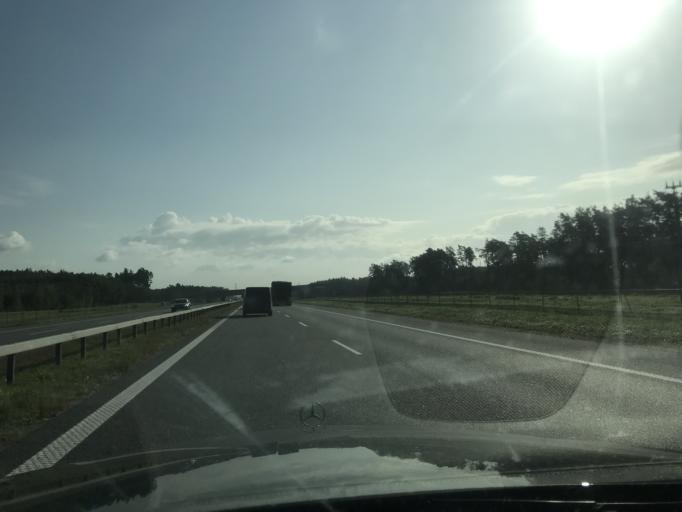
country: PL
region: Lesser Poland Voivodeship
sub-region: Powiat tarnowski
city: Wierzchoslawice
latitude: 50.0068
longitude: 20.8071
